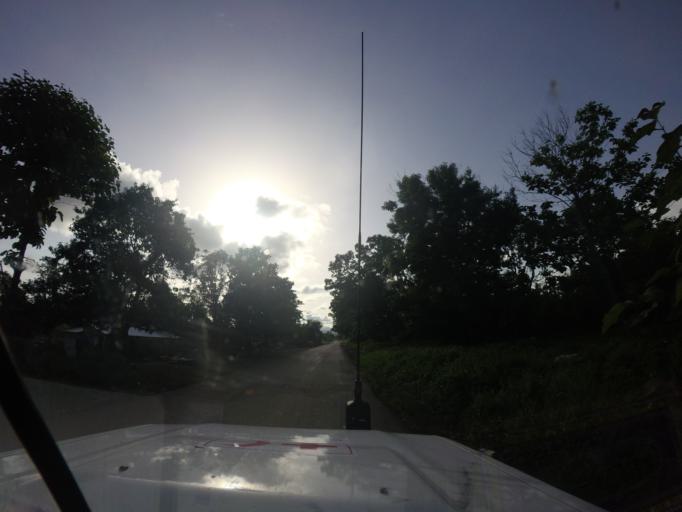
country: GN
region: Kindia
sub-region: Kindia
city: Kindia
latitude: 9.9974
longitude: -12.7556
